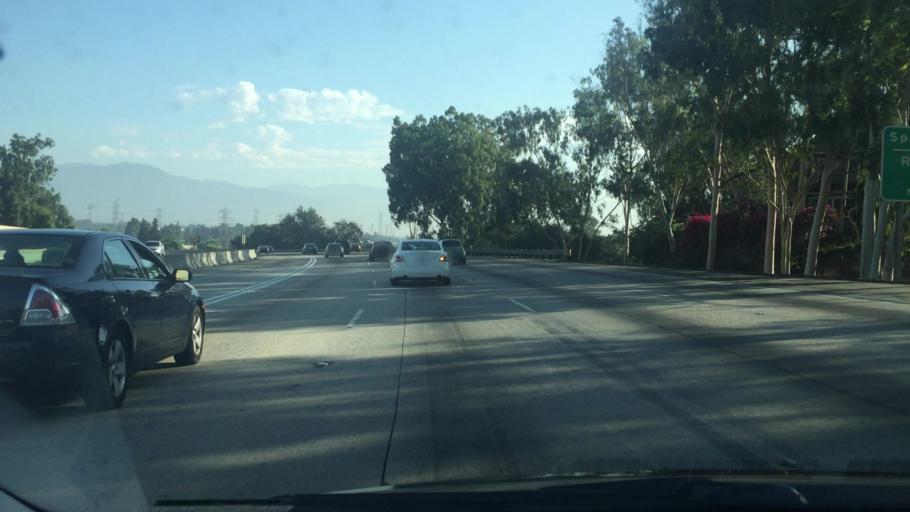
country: US
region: California
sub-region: Los Angeles County
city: West Whittier-Los Nietos
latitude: 34.0091
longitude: -118.0580
